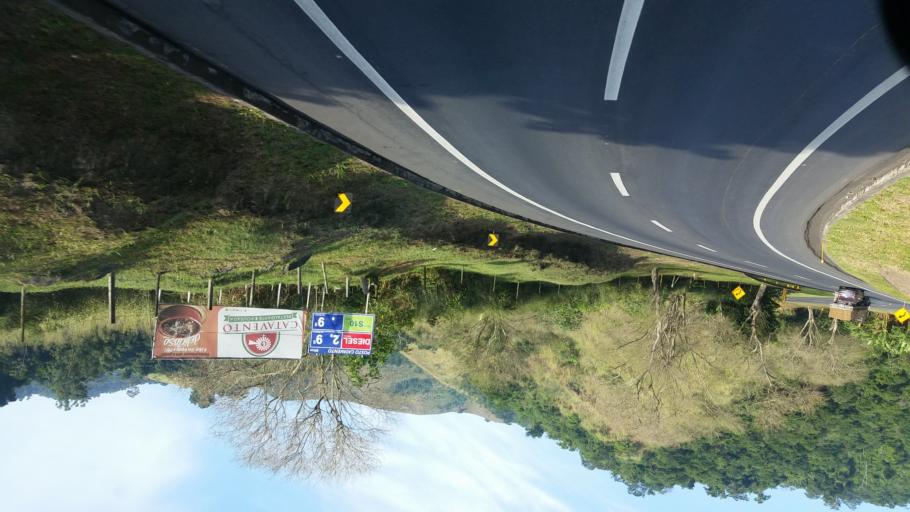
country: BR
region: Rio de Janeiro
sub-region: Pirai
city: Pirai
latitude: -22.6604
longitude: -43.8256
